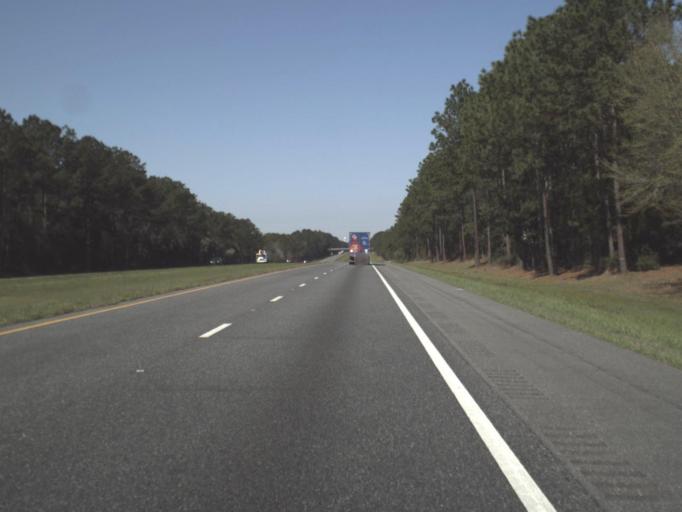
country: US
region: Florida
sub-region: Walton County
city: DeFuniak Springs
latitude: 30.6911
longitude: -86.0595
